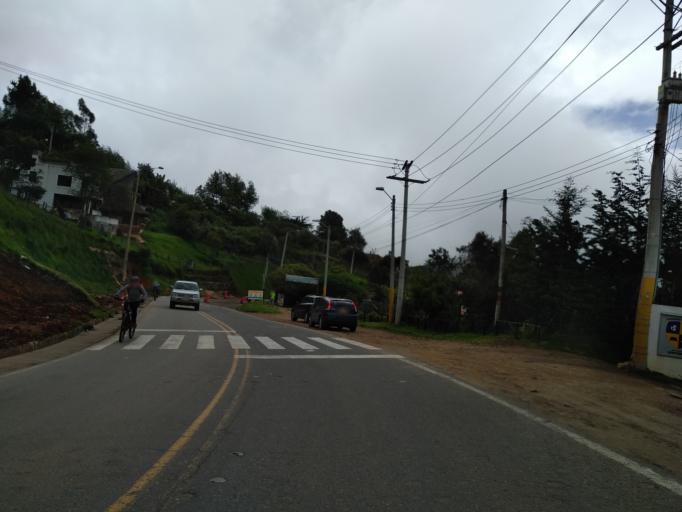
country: CO
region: Bogota D.C.
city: Barrio San Luis
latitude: 4.6615
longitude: -74.0081
